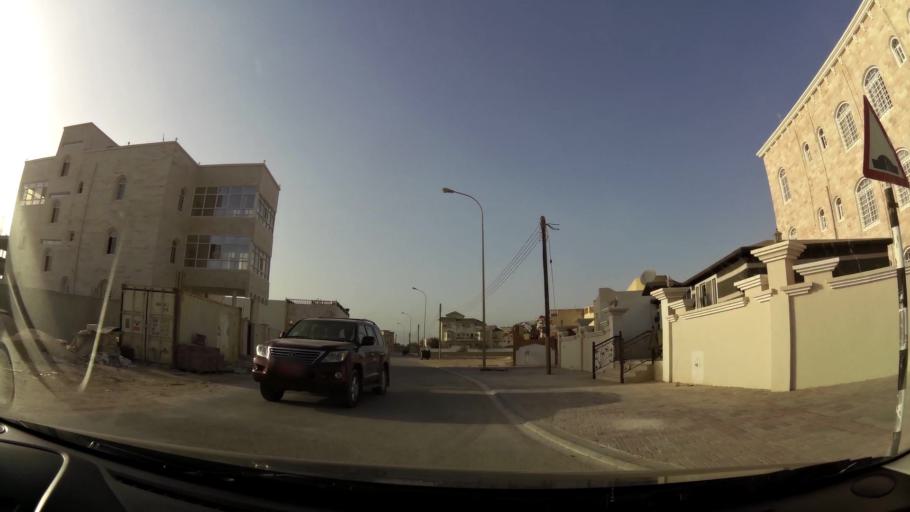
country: OM
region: Zufar
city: Salalah
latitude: 17.0000
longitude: 54.0277
